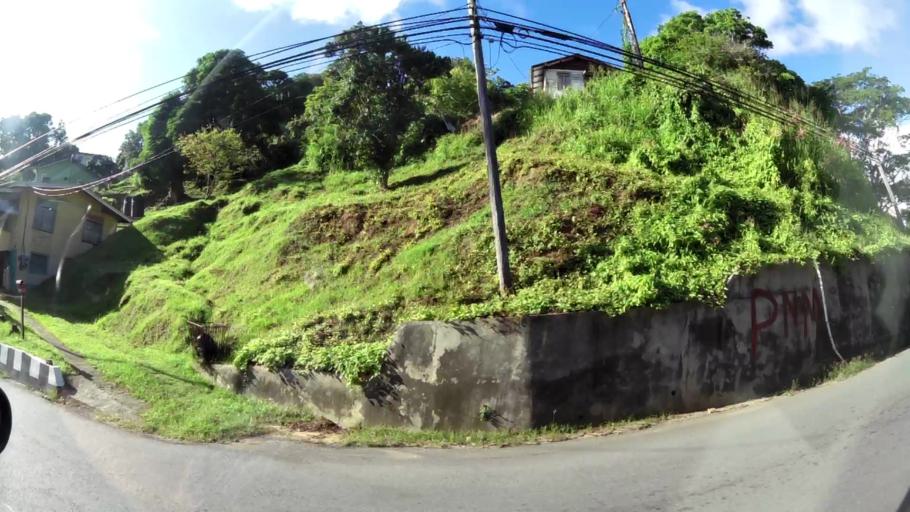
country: TT
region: Eastern Tobago
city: Roxborough
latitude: 11.2212
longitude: -60.6142
